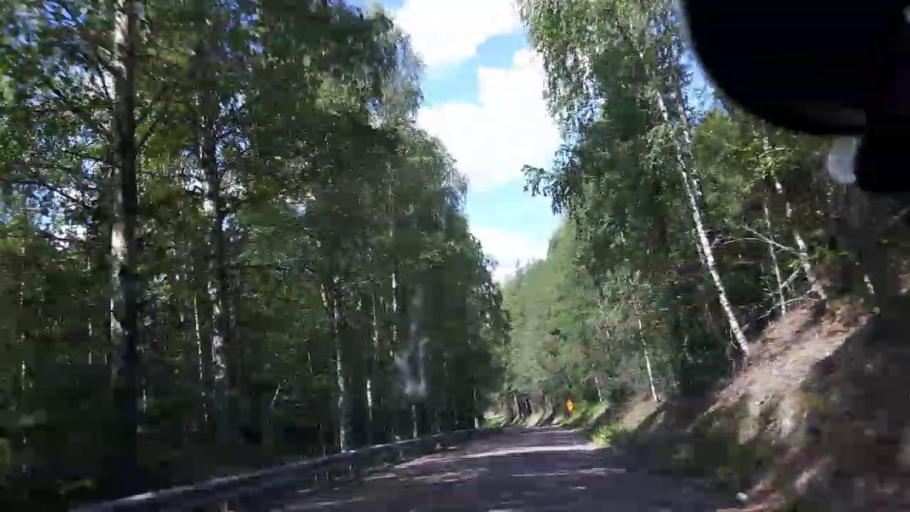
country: SE
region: Jaemtland
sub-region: Ragunda Kommun
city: Hammarstrand
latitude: 63.0117
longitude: 16.6371
